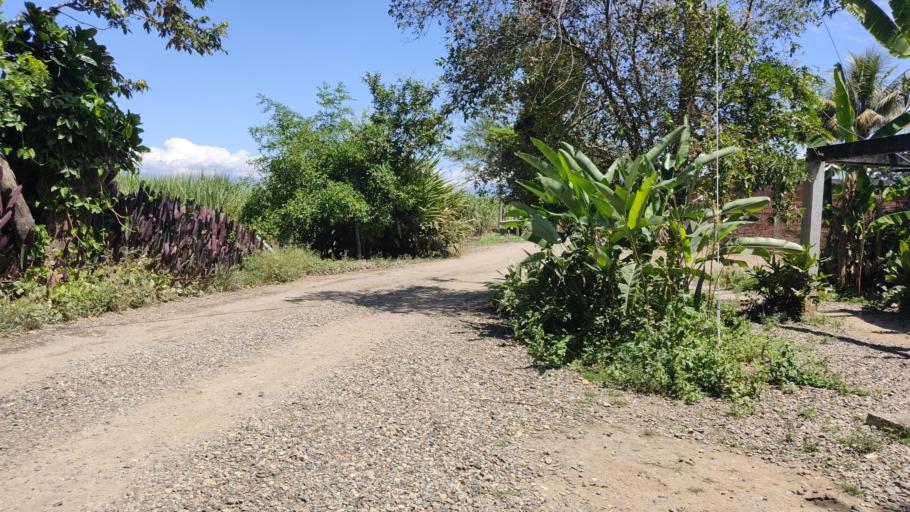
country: CO
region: Valle del Cauca
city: Jamundi
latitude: 3.1558
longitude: -76.5103
